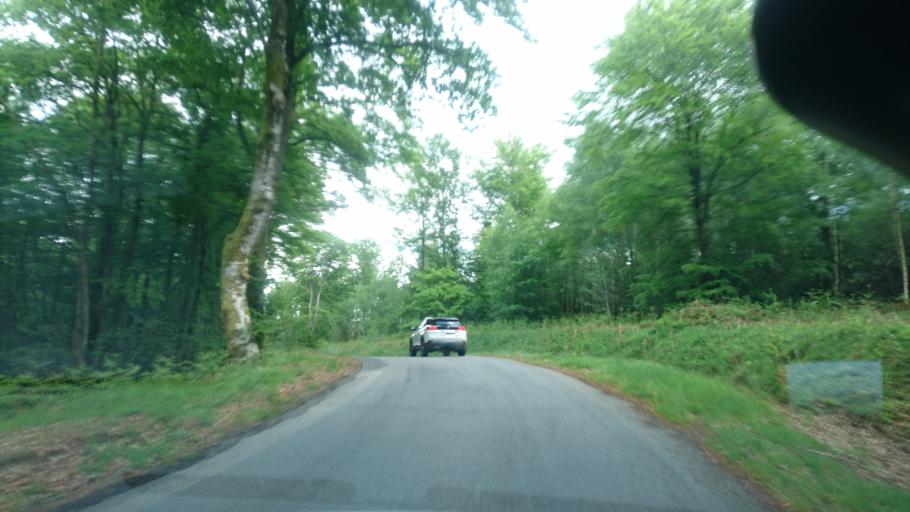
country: FR
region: Limousin
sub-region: Departement de la Haute-Vienne
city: Peyrat-le-Chateau
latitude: 45.7860
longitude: 1.9058
